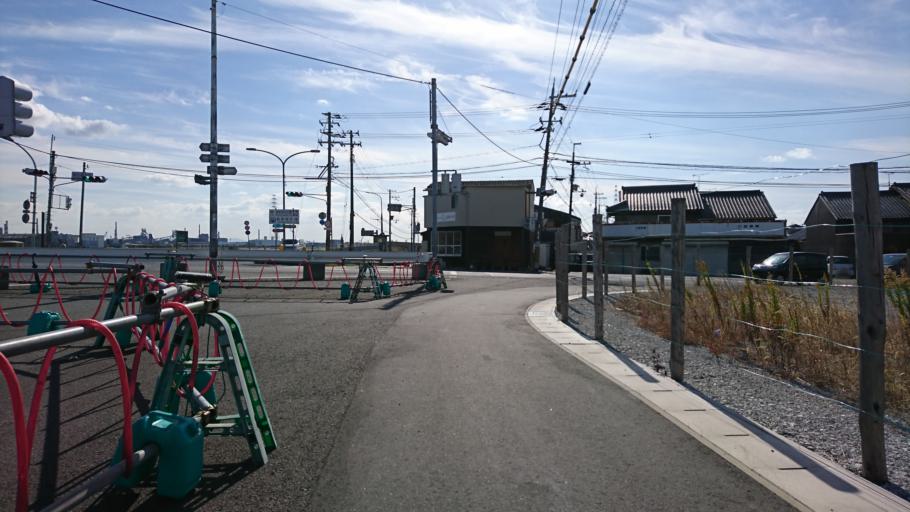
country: JP
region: Hyogo
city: Kakogawacho-honmachi
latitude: 34.7479
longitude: 134.8075
